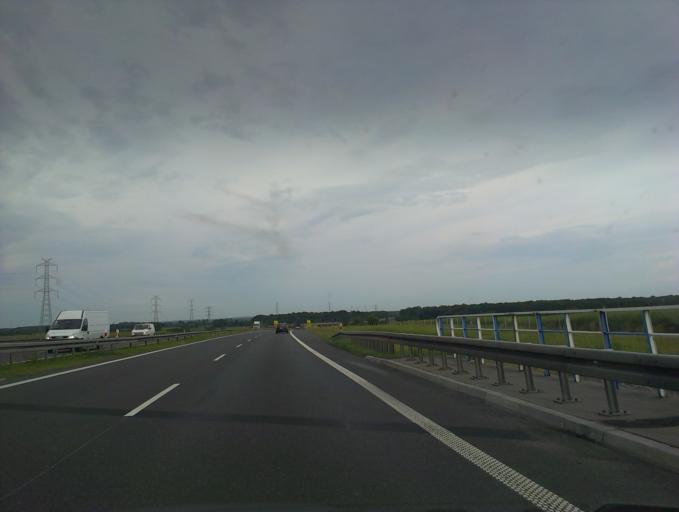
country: PL
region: Opole Voivodeship
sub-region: Powiat brzeski
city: Olszanka
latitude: 50.7354
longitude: 17.4912
